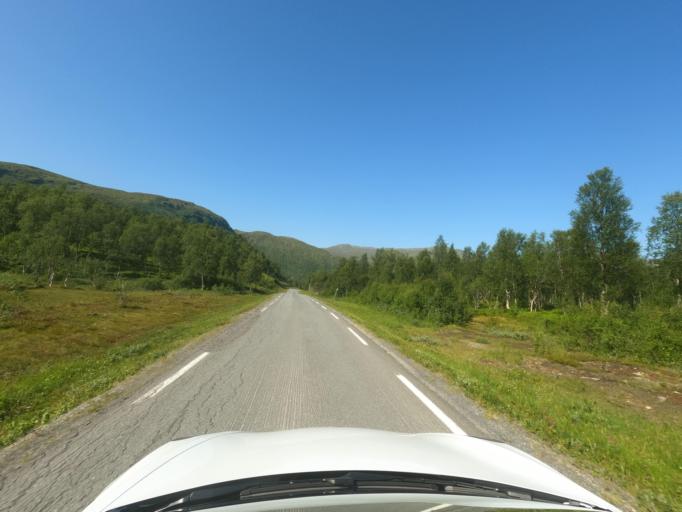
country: NO
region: Troms
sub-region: Skanland
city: Evenskjer
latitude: 68.3284
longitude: 16.5666
